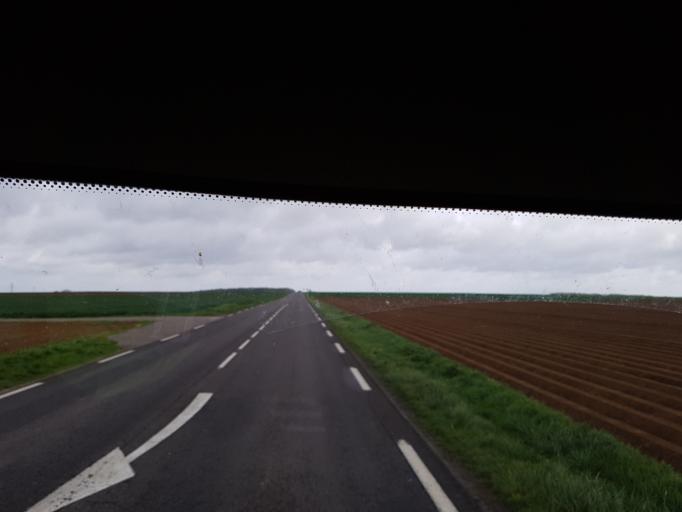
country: FR
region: Picardie
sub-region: Departement de l'Aisne
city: Crouy
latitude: 49.4222
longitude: 3.3474
